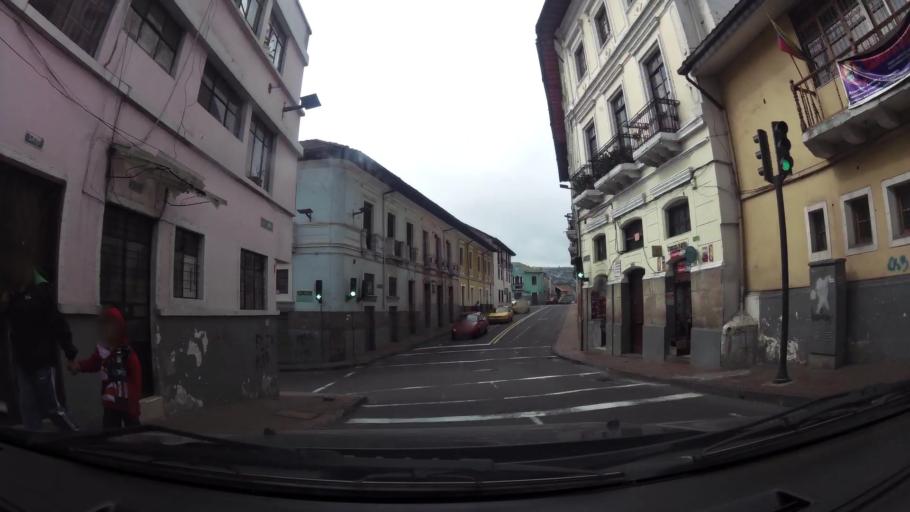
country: EC
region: Pichincha
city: Quito
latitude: -0.2251
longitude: -78.5161
